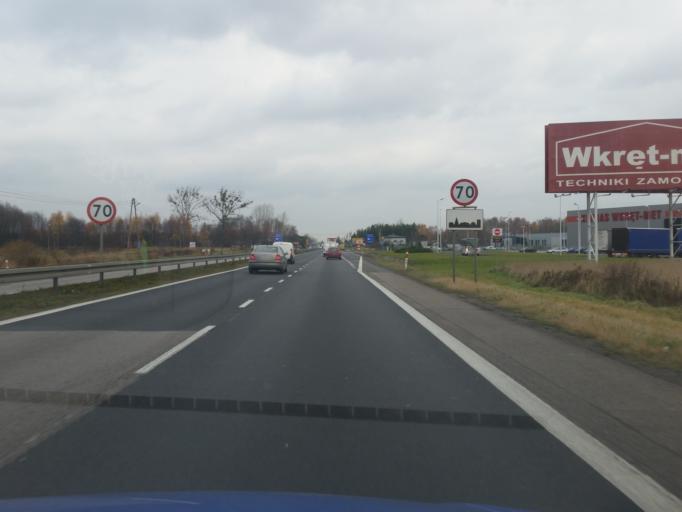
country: PL
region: Silesian Voivodeship
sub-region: Powiat czestochowski
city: Kamienica Polska
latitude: 50.6852
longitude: 19.1315
